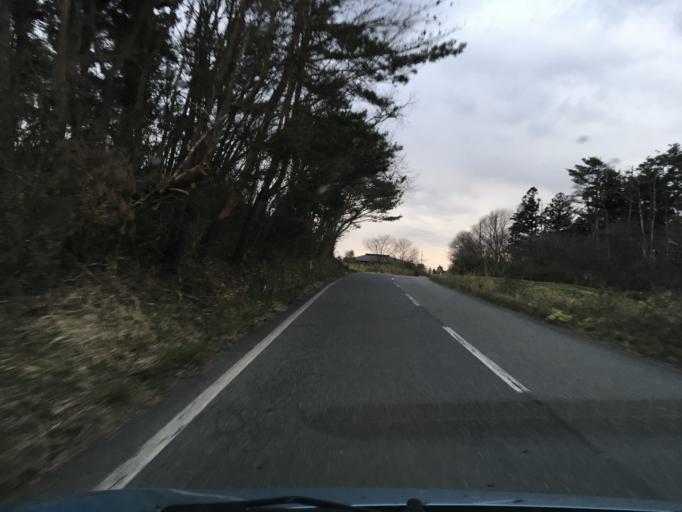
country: JP
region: Iwate
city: Ichinoseki
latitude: 38.7785
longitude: 141.2447
